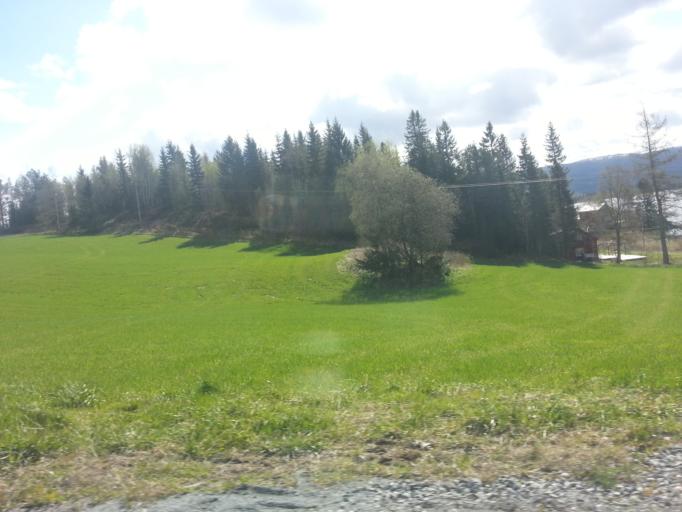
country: NO
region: Nord-Trondelag
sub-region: Levanger
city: Skogn
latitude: 63.6397
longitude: 11.2433
